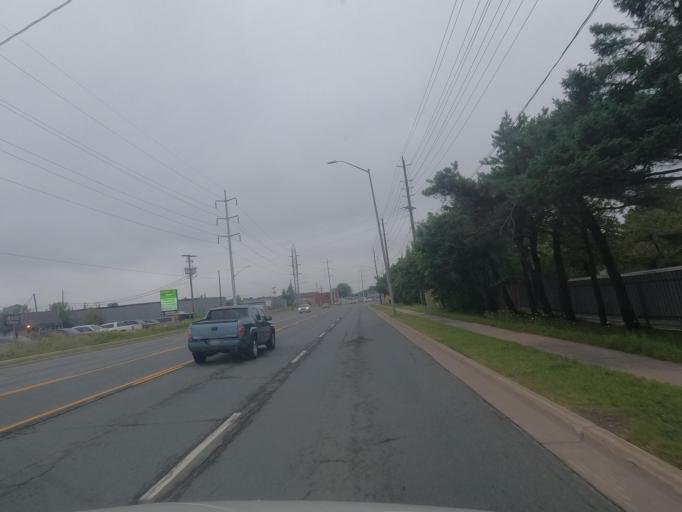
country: CA
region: Ontario
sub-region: Algoma
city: Sault Ste. Marie
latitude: 46.5383
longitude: -84.3305
